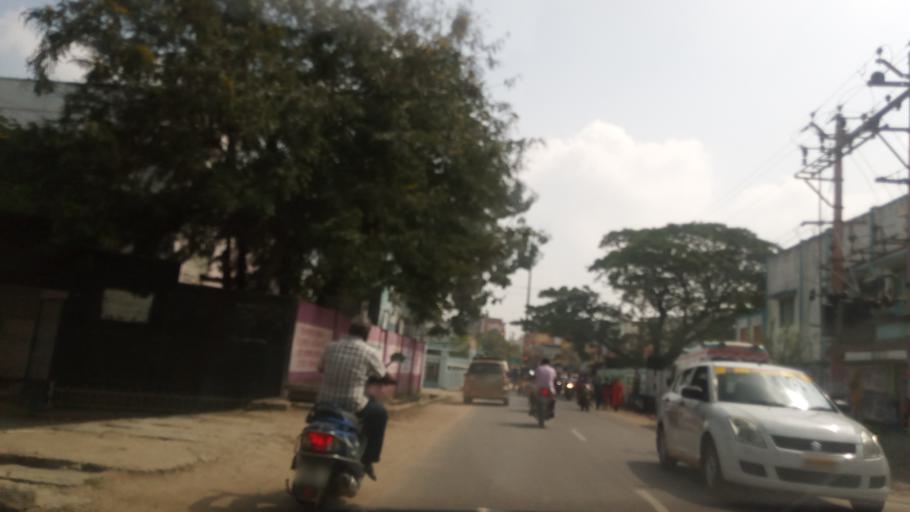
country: IN
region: Tamil Nadu
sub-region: Vellore
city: Arakkonam
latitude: 13.0852
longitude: 79.6653
